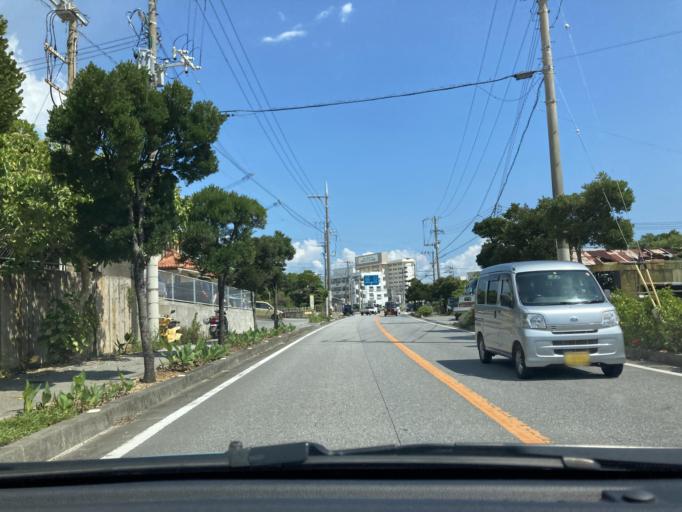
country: JP
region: Okinawa
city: Ginowan
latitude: 26.1837
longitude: 127.7729
